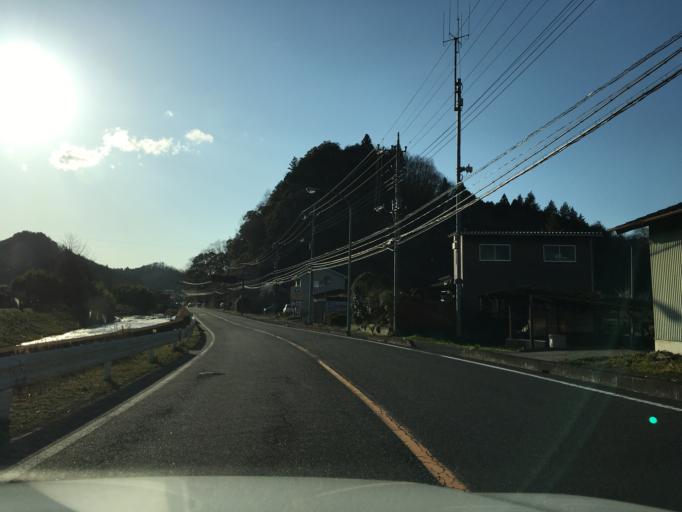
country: JP
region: Ibaraki
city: Daigo
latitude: 36.7785
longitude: 140.2951
